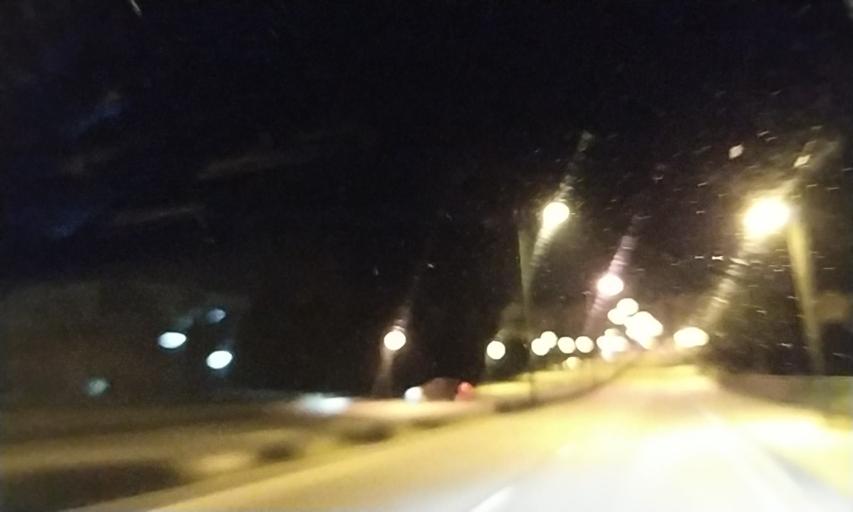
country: PT
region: Castelo Branco
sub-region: Concelho do Fundao
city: Fundao
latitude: 40.1430
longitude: -7.5029
